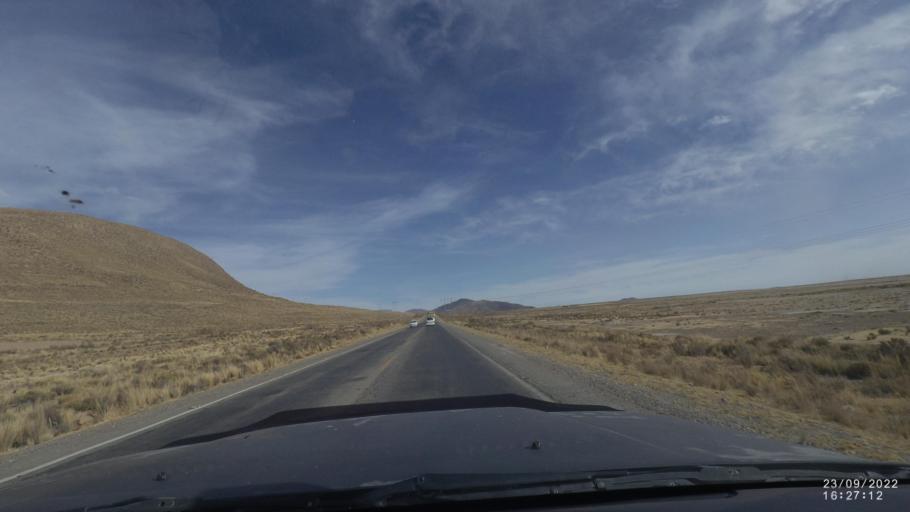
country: BO
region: Oruro
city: Machacamarca
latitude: -18.1146
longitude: -67.0042
